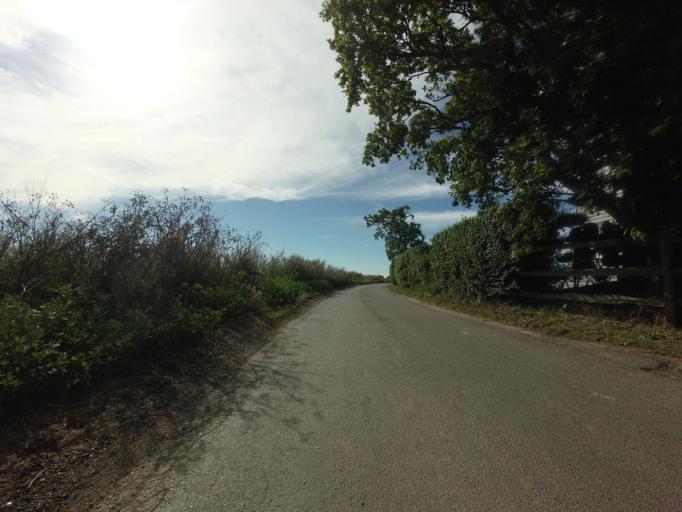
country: GB
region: England
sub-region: Kent
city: Herne Bay
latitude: 51.3662
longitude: 1.1940
